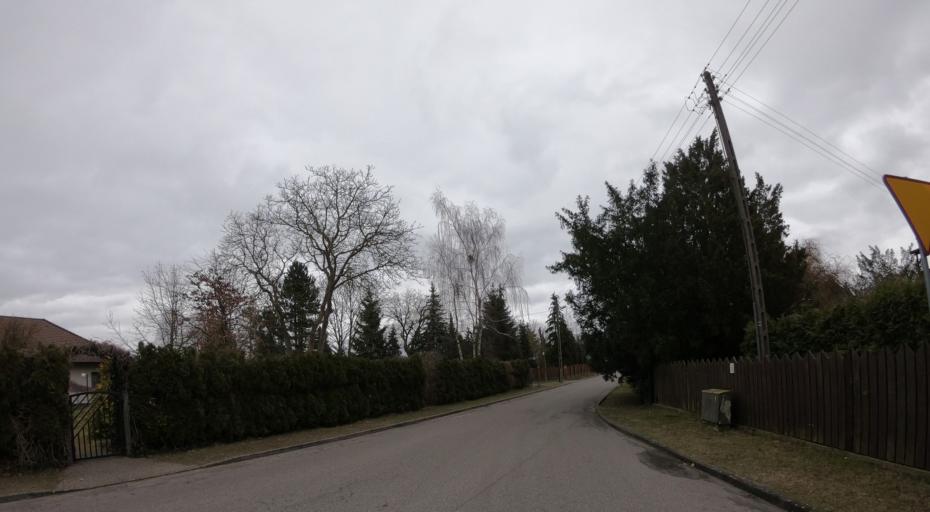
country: PL
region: West Pomeranian Voivodeship
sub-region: Powiat goleniowski
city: Stepnica
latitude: 53.6625
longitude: 14.4979
